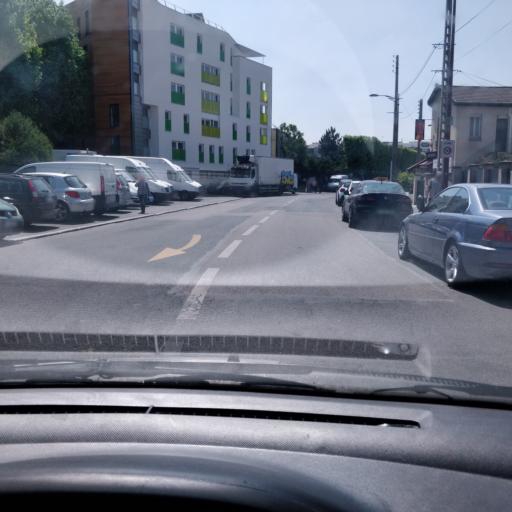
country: FR
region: Ile-de-France
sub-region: Departement de Seine-Saint-Denis
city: Bondy
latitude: 48.9153
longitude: 2.4841
